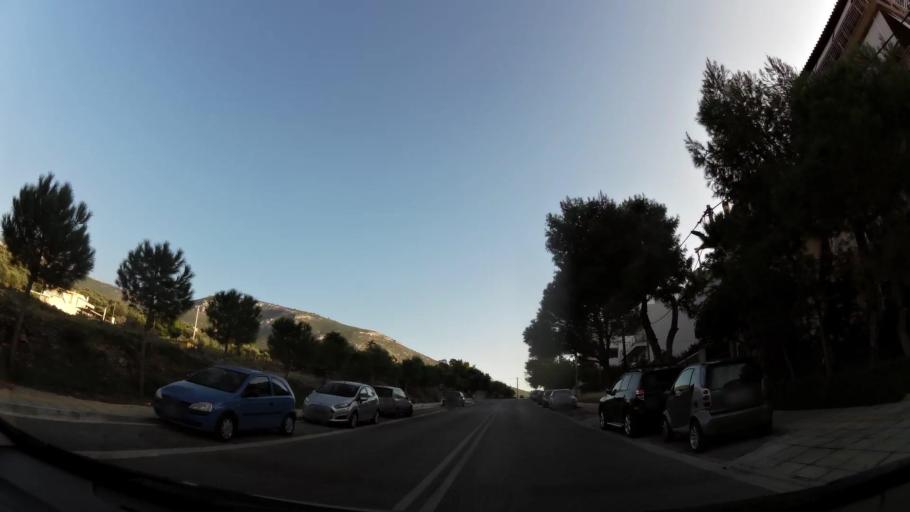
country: GR
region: Attica
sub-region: Nomarchia Athinas
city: Argyroupoli
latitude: 37.8926
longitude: 23.7767
